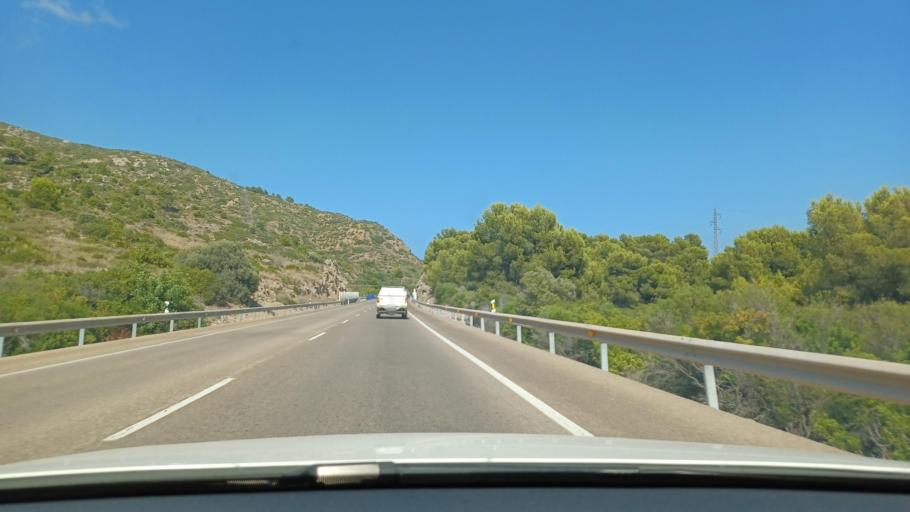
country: ES
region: Valencia
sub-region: Provincia de Castello
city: Benicassim
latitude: 40.0699
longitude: 0.0994
